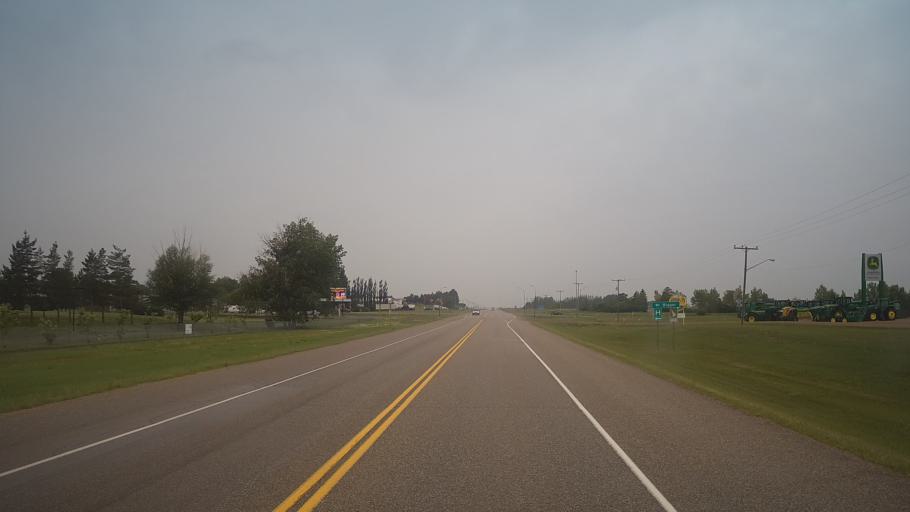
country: CA
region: Saskatchewan
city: Biggar
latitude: 52.0616
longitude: -107.9758
